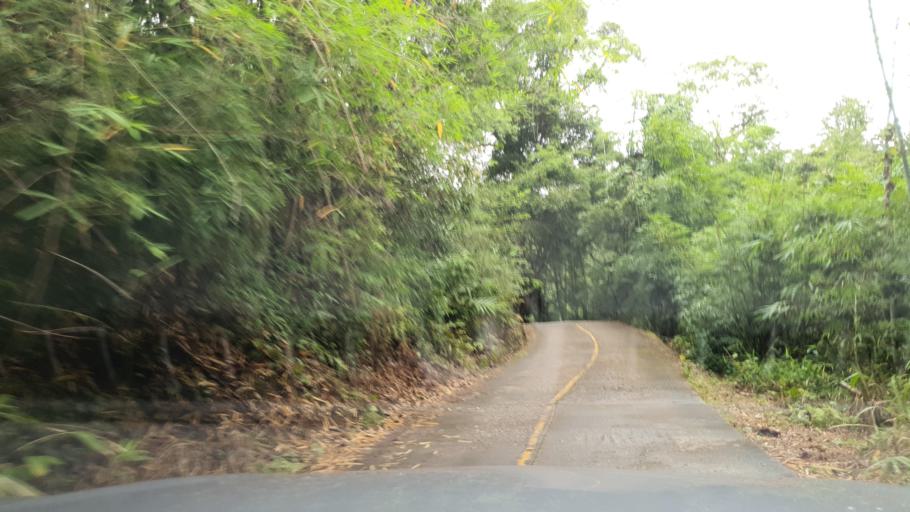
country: TH
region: Chiang Mai
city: Mae Taeng
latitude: 19.2214
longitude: 98.9250
